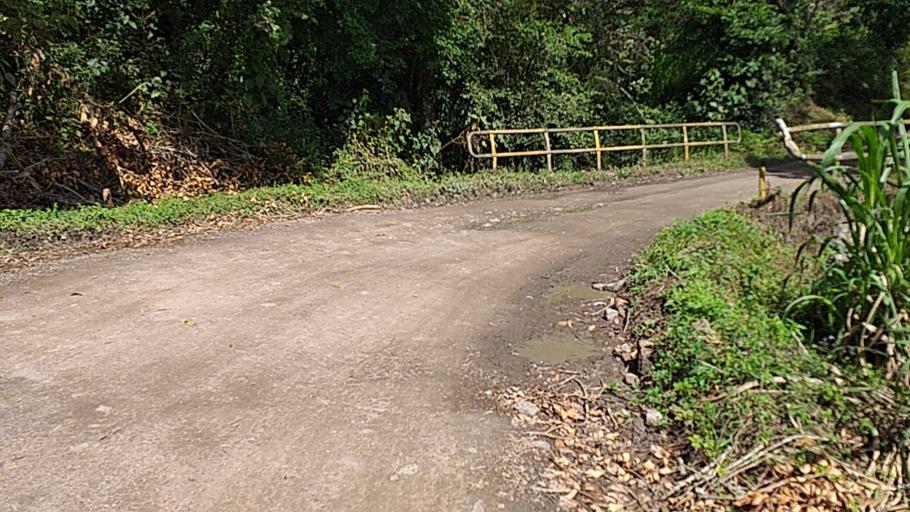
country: CO
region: Cundinamarca
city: Tenza
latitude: 5.1006
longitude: -73.4509
